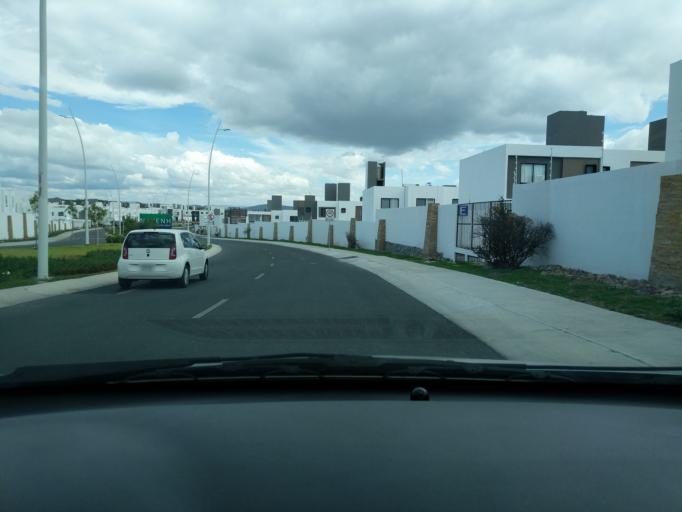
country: MX
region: Queretaro
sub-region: El Marques
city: El Pozo
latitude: 20.6491
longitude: -100.3156
